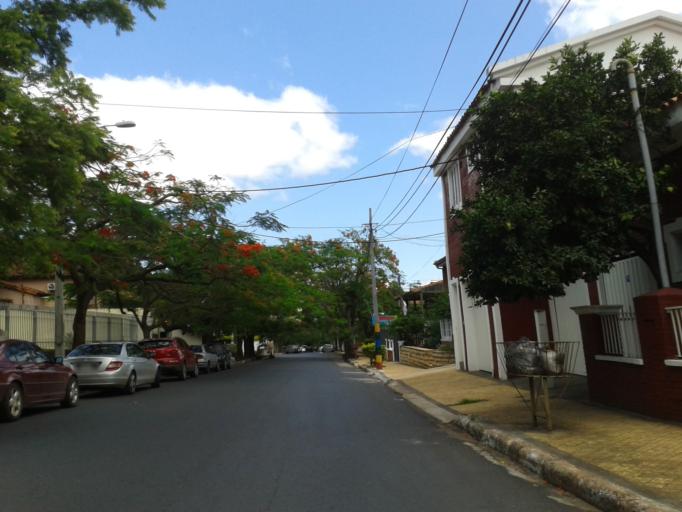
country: PY
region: Asuncion
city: Asuncion
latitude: -25.2925
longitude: -57.6165
